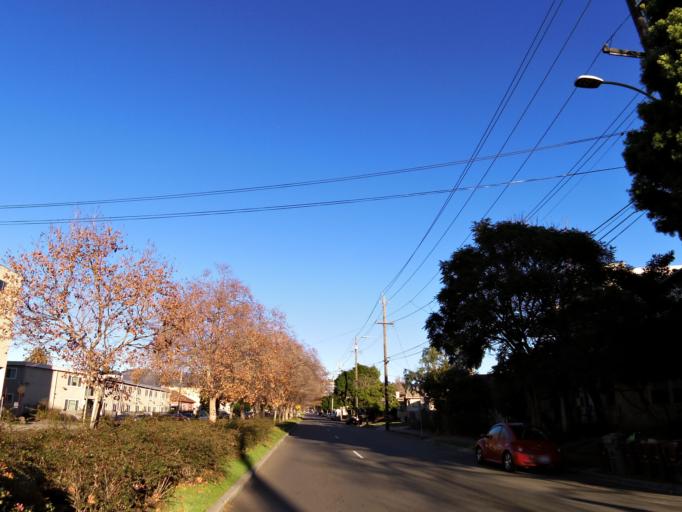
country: US
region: California
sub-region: Alameda County
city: Emeryville
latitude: 37.8411
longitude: -122.2827
